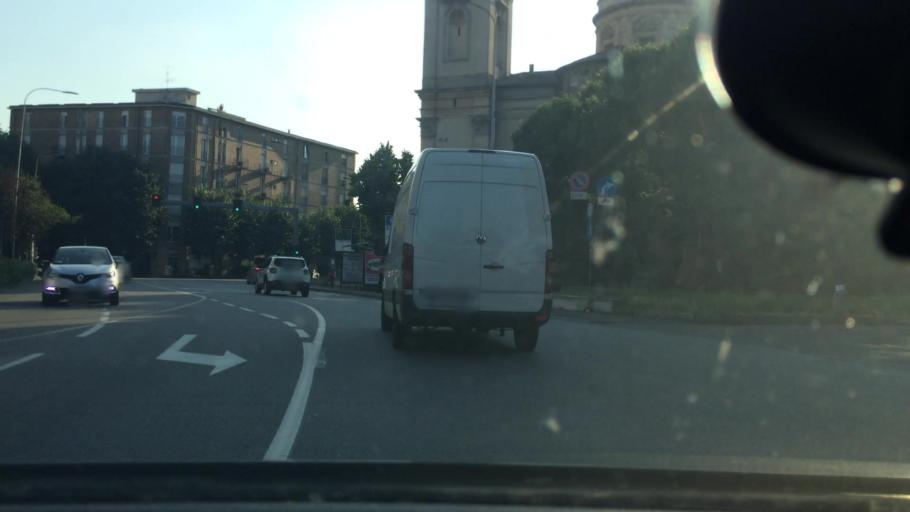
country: IT
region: Lombardy
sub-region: Citta metropolitana di Milano
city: Rho
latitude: 45.5331
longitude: 9.0406
